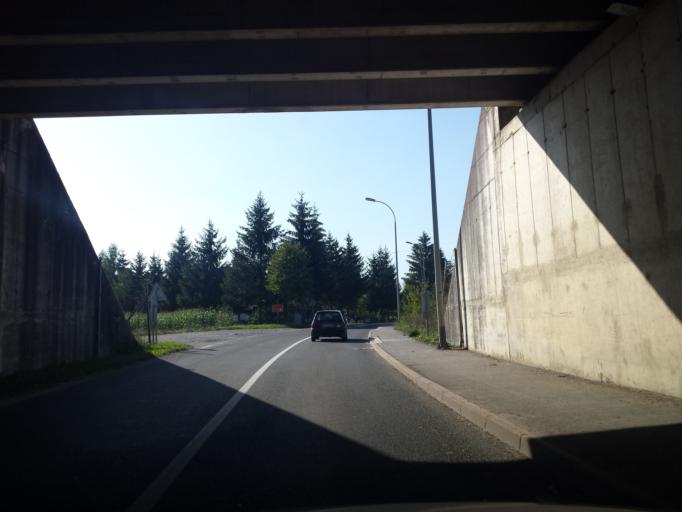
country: HR
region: Karlovacka
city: Ostarije
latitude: 45.2283
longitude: 15.2654
